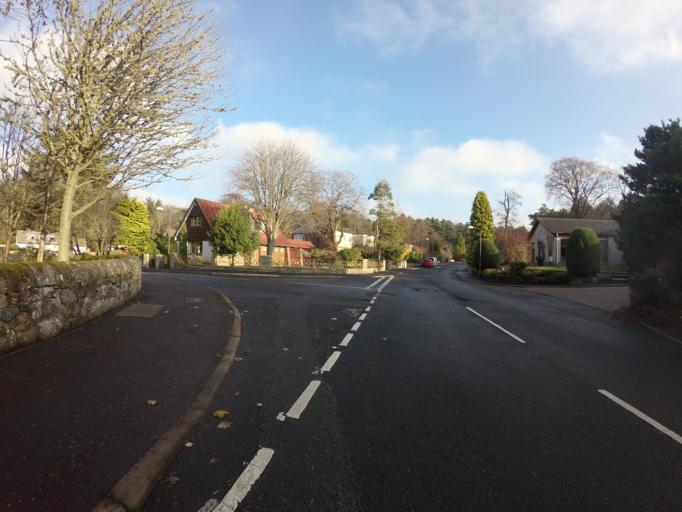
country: GB
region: Scotland
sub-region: West Lothian
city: Livingston
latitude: 55.9098
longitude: -3.5579
